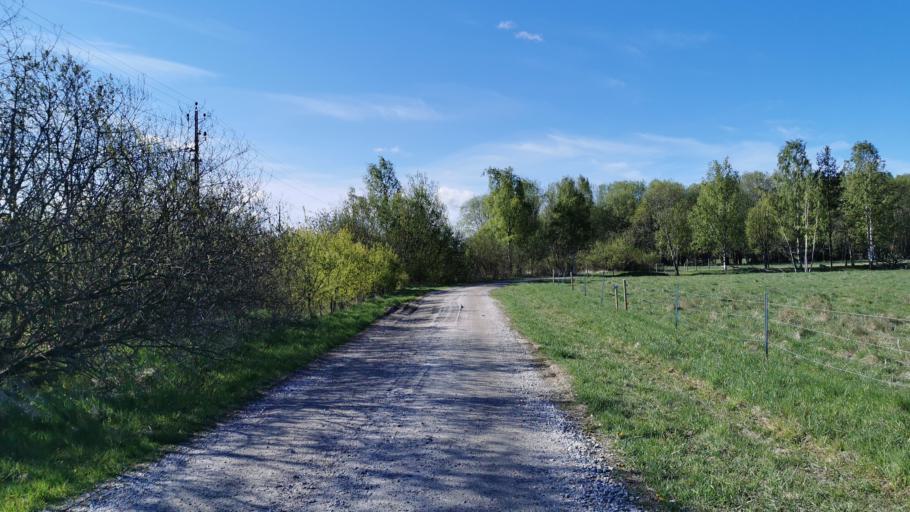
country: SE
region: OErebro
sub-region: Orebro Kommun
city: Orebro
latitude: 59.2993
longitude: 15.2211
